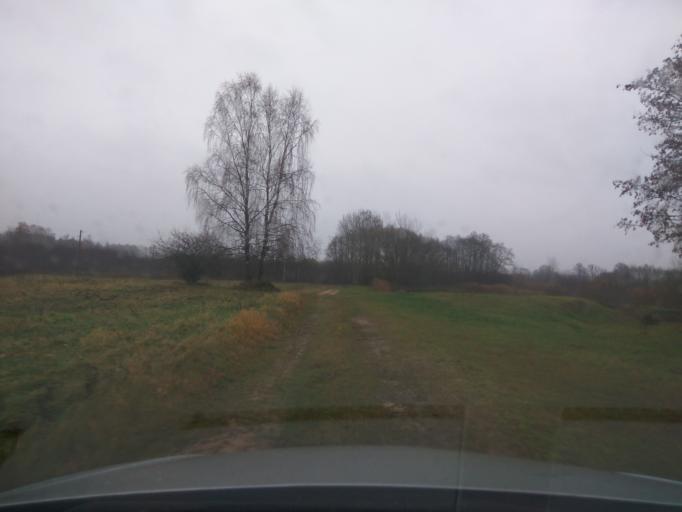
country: LV
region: Kuldigas Rajons
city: Kuldiga
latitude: 56.9240
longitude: 21.9708
